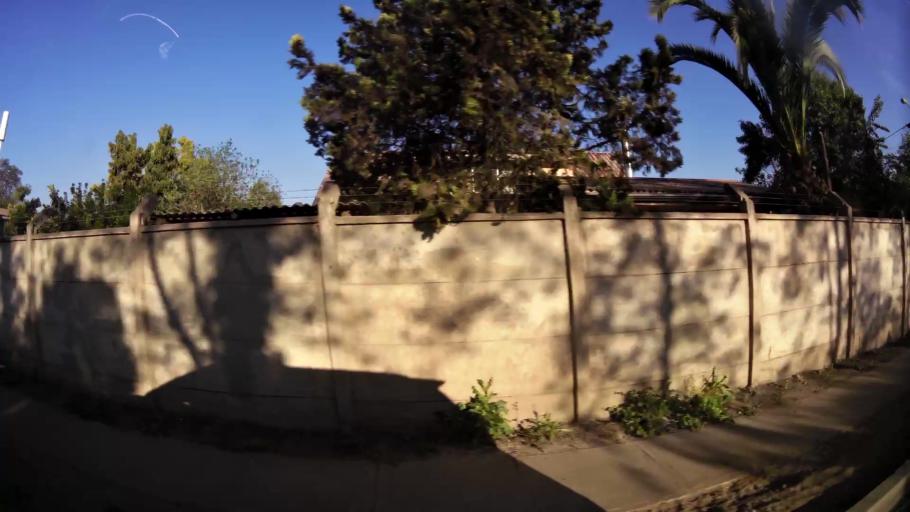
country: CL
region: Santiago Metropolitan
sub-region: Provincia de Talagante
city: Penaflor
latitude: -33.6182
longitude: -70.8652
